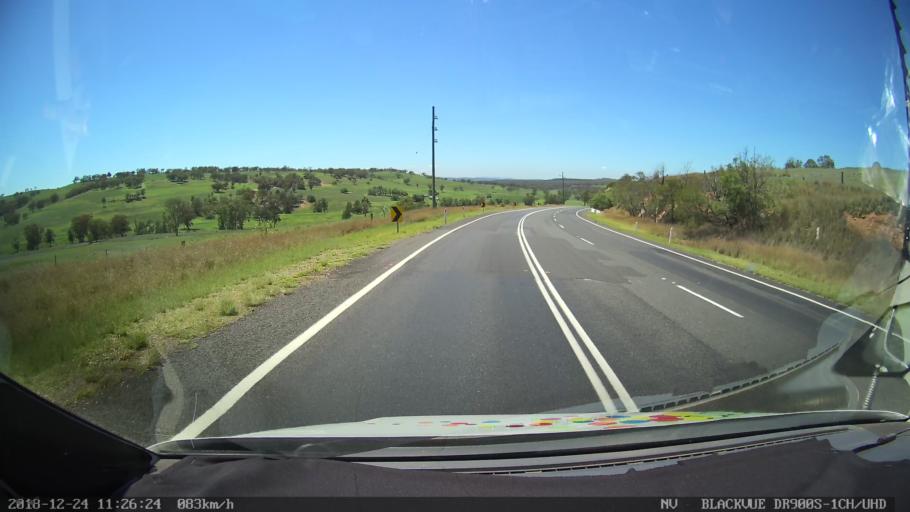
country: AU
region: New South Wales
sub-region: Upper Hunter Shire
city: Merriwa
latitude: -32.1691
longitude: 150.4310
